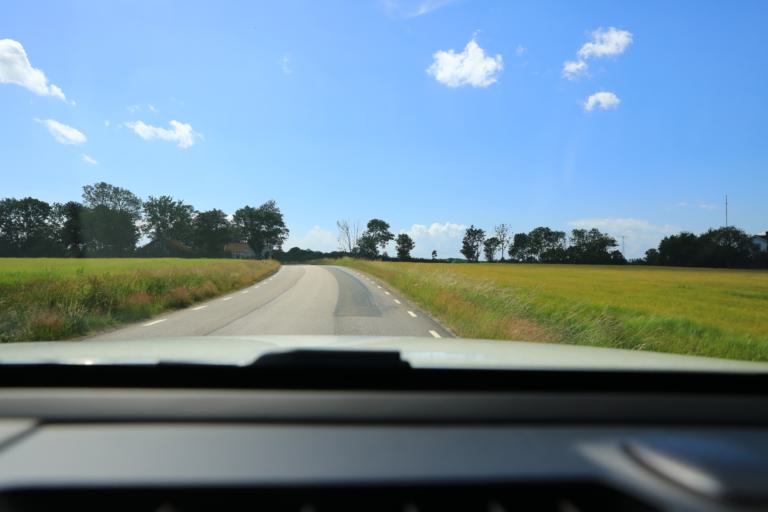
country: SE
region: Halland
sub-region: Varbergs Kommun
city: Tvaaker
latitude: 57.1120
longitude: 12.4246
